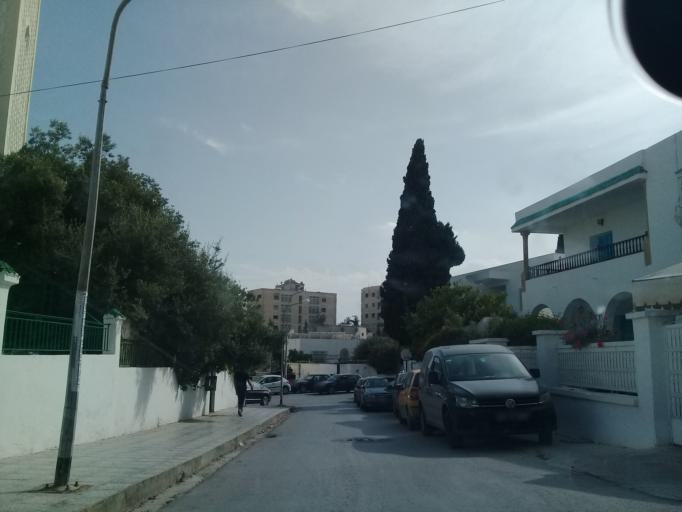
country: TN
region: Tunis
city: Tunis
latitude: 36.8472
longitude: 10.1644
